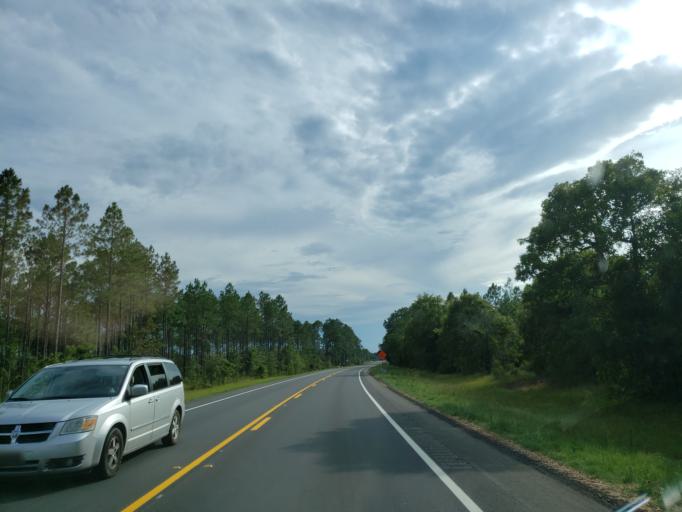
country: US
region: Georgia
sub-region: Berrien County
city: Enigma
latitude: 31.5409
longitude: -83.3866
